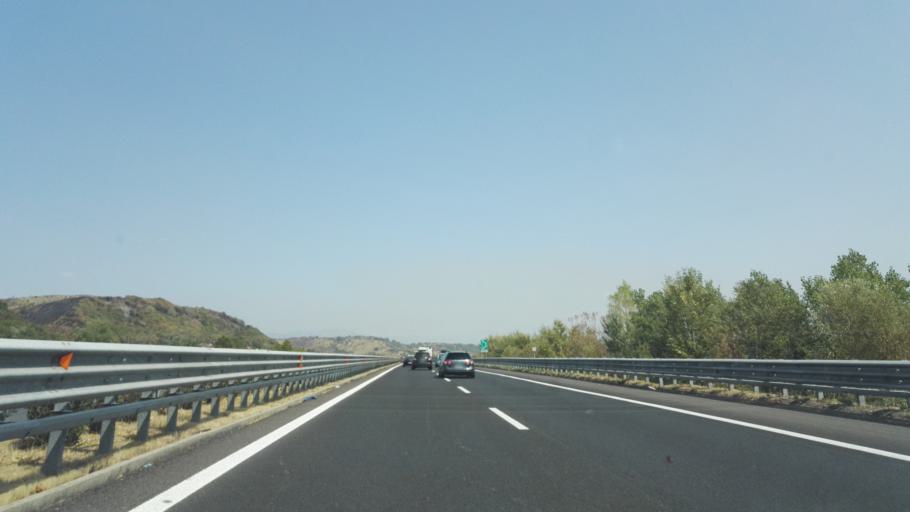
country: IT
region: Calabria
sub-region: Provincia di Cosenza
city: Sartano
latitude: 39.4792
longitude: 16.2154
